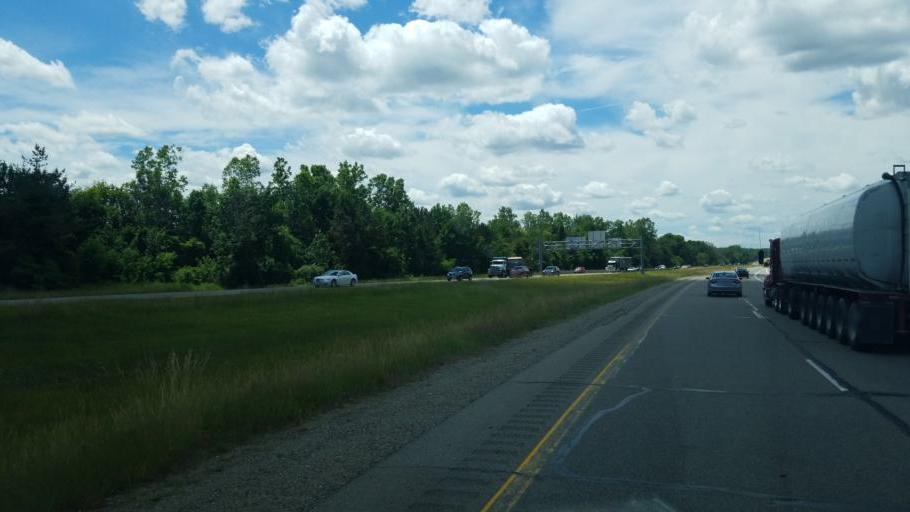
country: US
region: Michigan
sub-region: Ingham County
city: Holt
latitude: 42.6737
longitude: -84.4989
